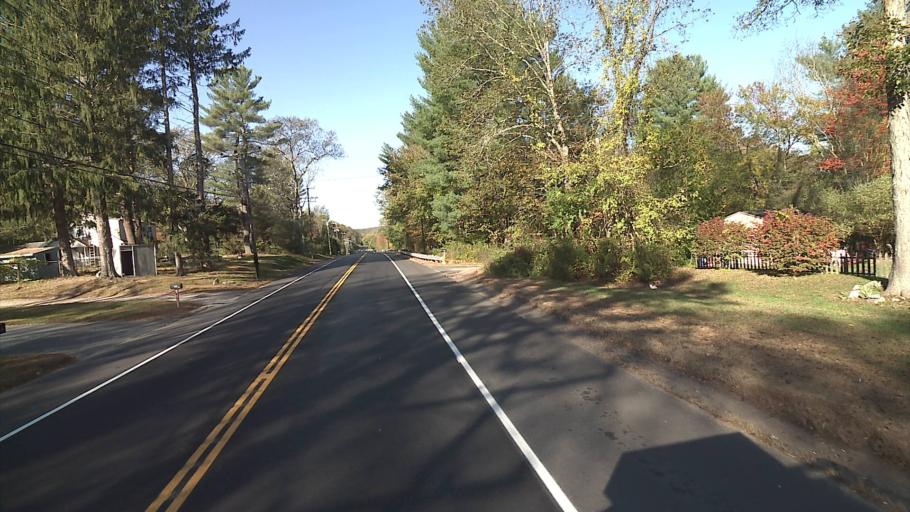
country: US
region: Connecticut
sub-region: Tolland County
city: South Coventry
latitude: 41.7235
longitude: -72.2977
